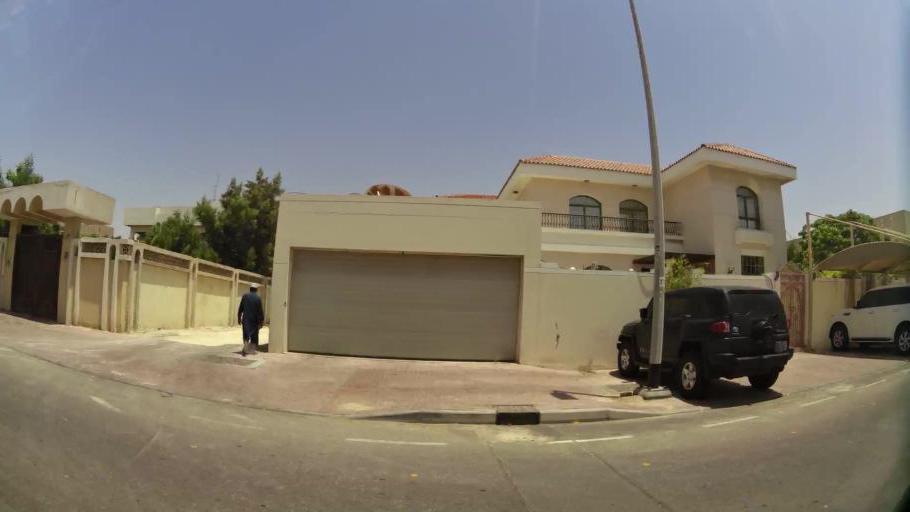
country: AE
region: Ash Shariqah
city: Sharjah
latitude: 25.2925
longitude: 55.3308
